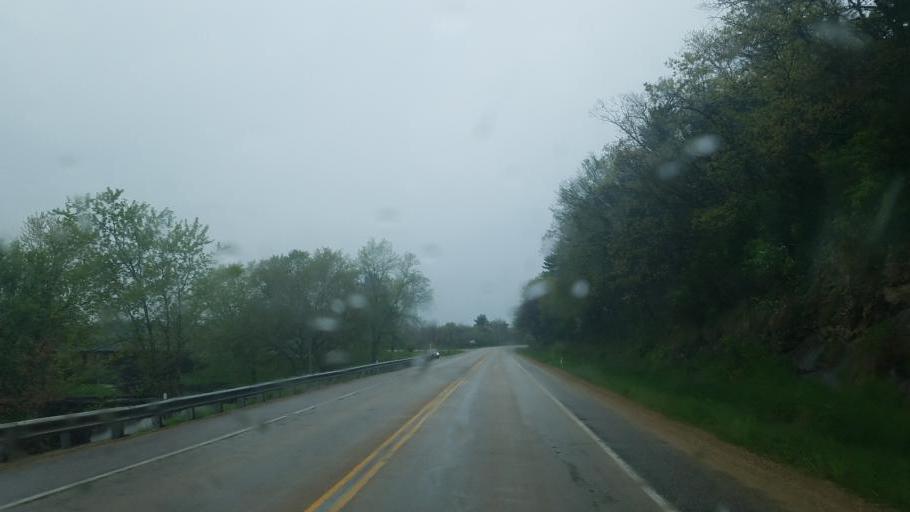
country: US
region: Wisconsin
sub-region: Juneau County
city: Elroy
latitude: 43.6401
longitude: -90.2094
